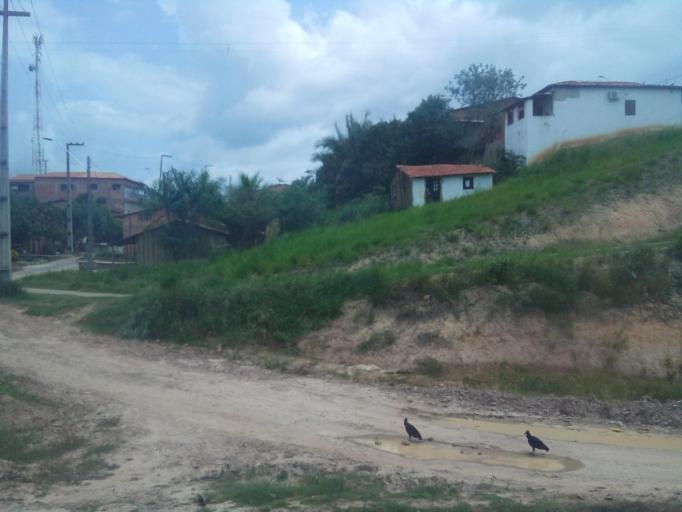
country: BR
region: Maranhao
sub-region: Santa Ines
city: Santa Ines
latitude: -3.6727
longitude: -45.8490
